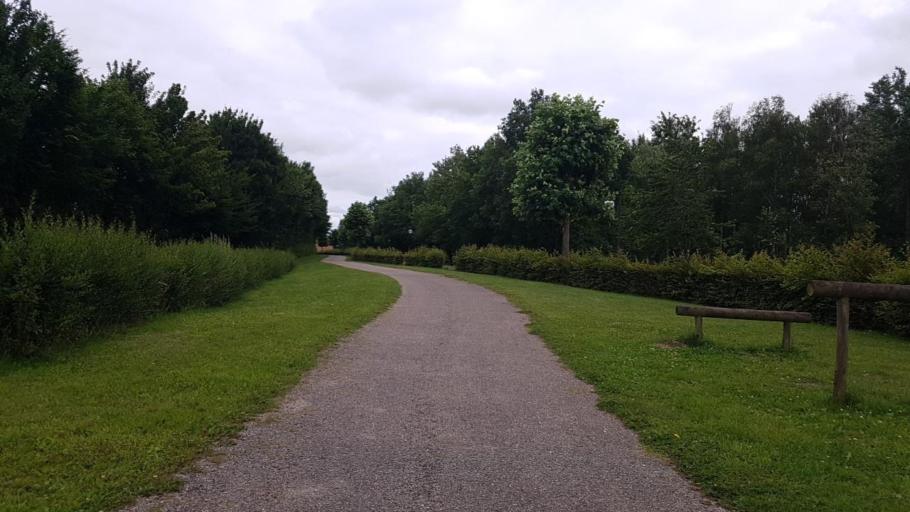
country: FR
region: Picardie
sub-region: Departement de l'Aisne
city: Hirson
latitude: 49.9125
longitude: 4.0598
